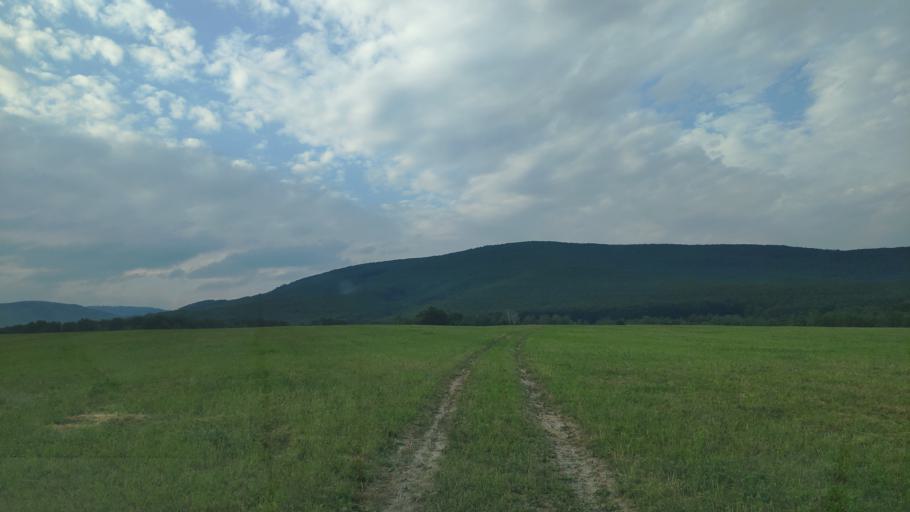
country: SK
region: Kosicky
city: Moldava nad Bodvou
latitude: 48.7119
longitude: 20.9934
